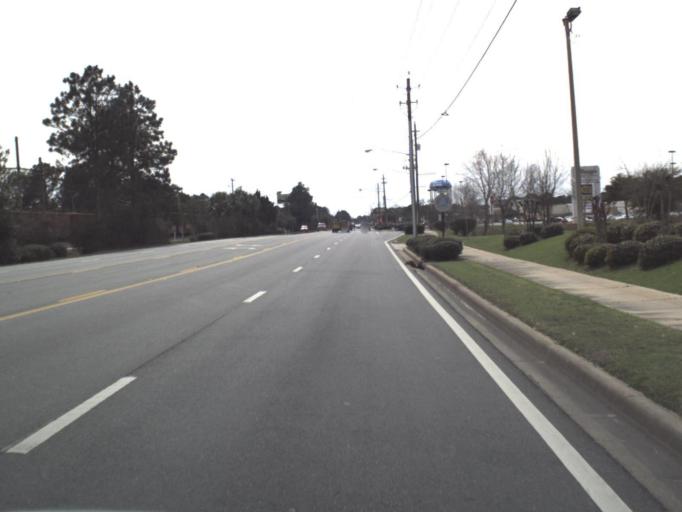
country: US
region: Florida
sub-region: Bay County
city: Hiland Park
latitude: 30.1880
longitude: -85.6431
